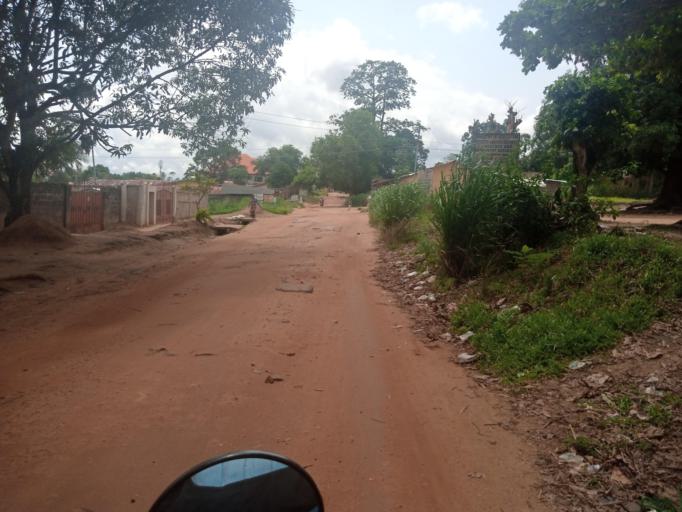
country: SL
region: Southern Province
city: Bo
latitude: 7.9642
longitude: -11.7465
